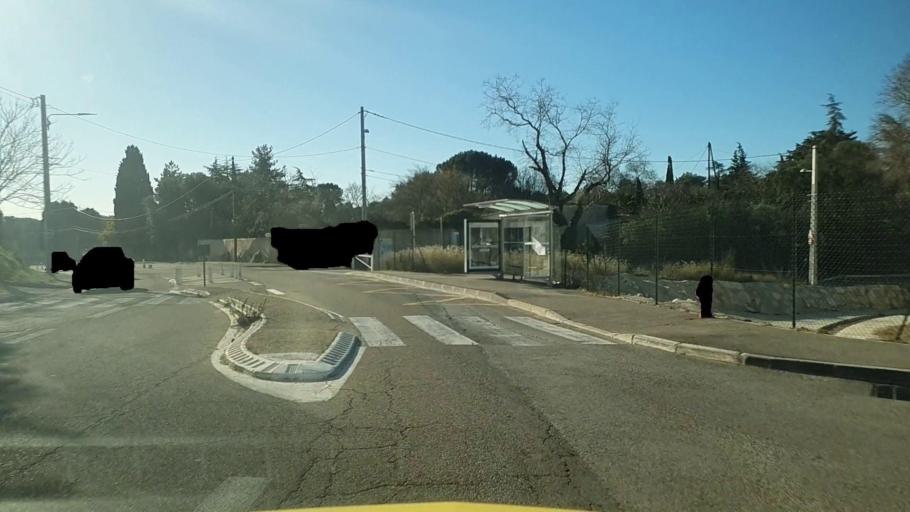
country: FR
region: Languedoc-Roussillon
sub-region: Departement du Gard
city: Nimes
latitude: 43.8561
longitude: 4.3371
